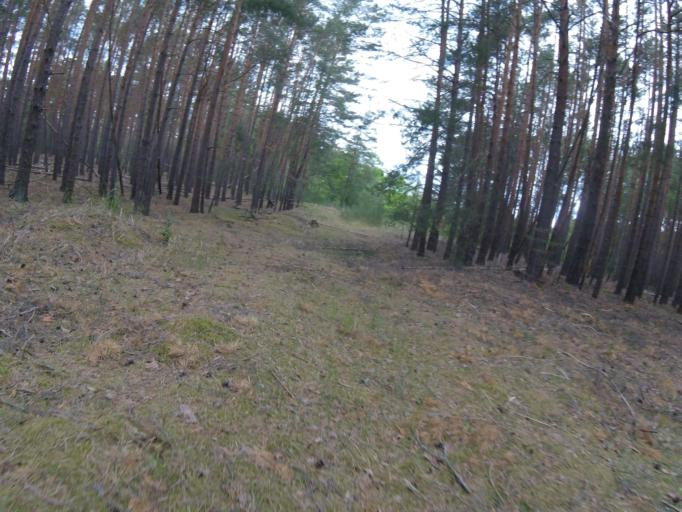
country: DE
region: Brandenburg
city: Halbe
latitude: 52.1687
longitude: 13.7531
